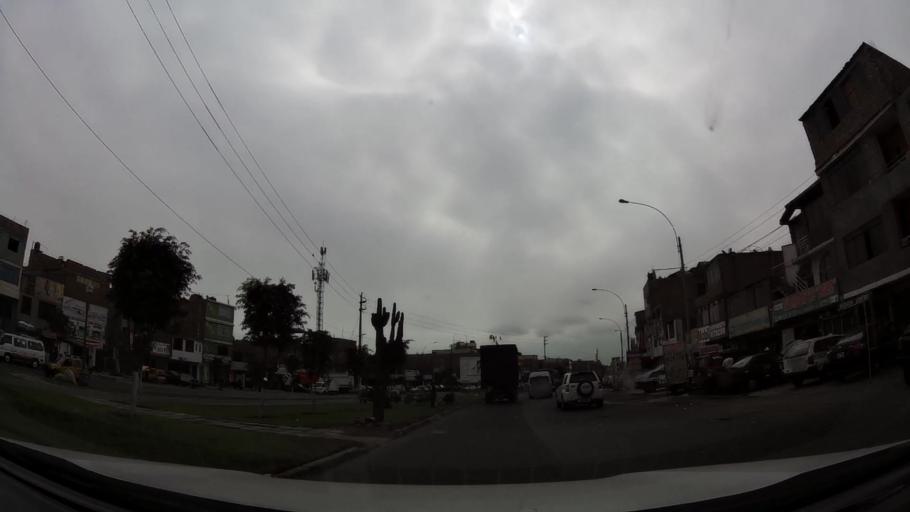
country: PE
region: Callao
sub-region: Callao
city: Callao
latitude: -12.0293
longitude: -77.0961
